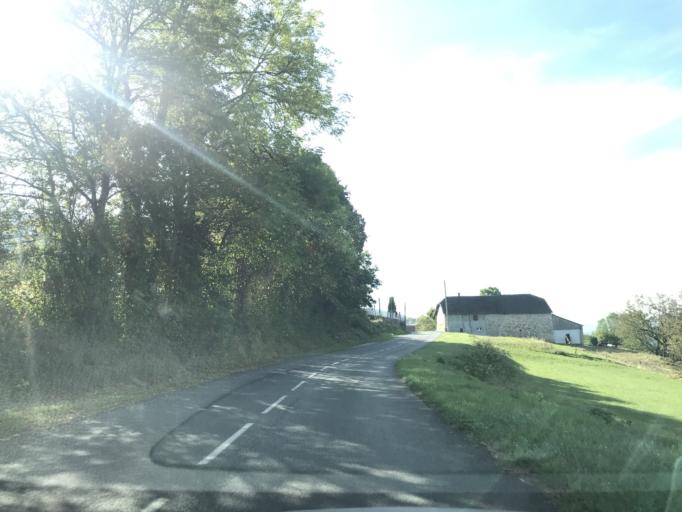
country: FR
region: Rhone-Alpes
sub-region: Departement de la Savoie
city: Yenne
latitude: 45.6542
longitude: 5.7892
